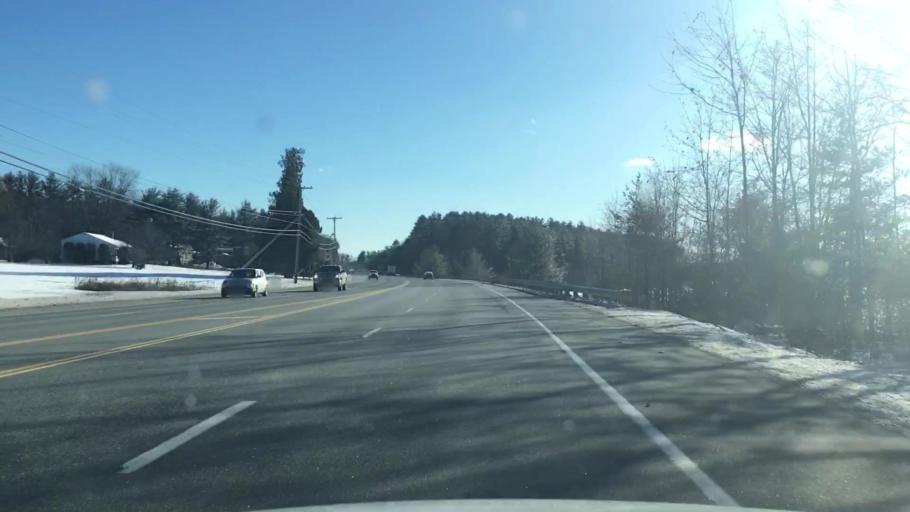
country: US
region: Maine
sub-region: Androscoggin County
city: Auburn
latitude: 44.1550
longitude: -70.2331
